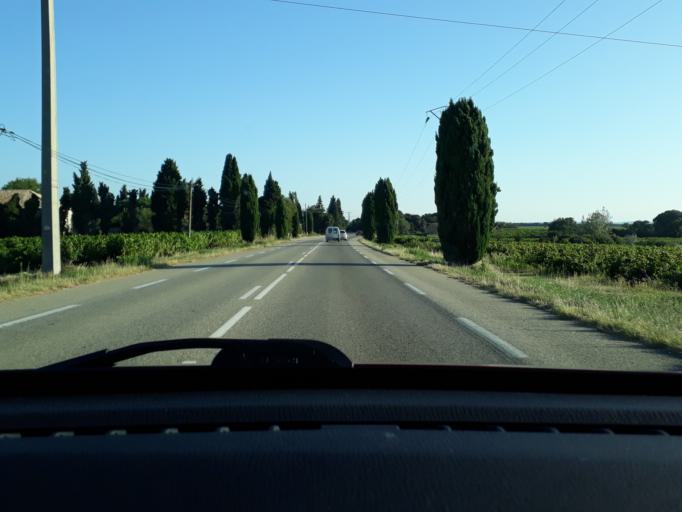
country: FR
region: Provence-Alpes-Cote d'Azur
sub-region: Departement du Vaucluse
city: Sainte-Cecile-les-Vignes
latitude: 44.2166
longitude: 4.9342
